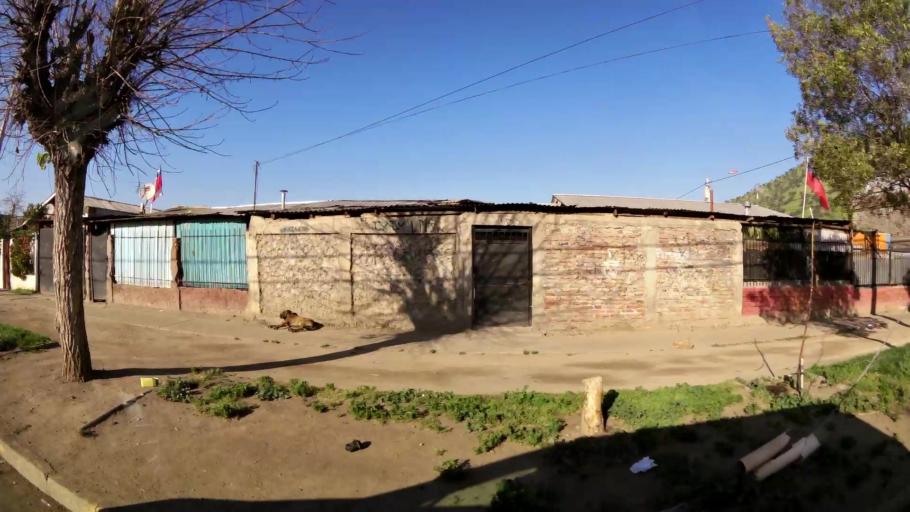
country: CL
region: Santiago Metropolitan
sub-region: Provincia de Chacabuco
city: Chicureo Abajo
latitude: -33.3635
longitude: -70.6353
